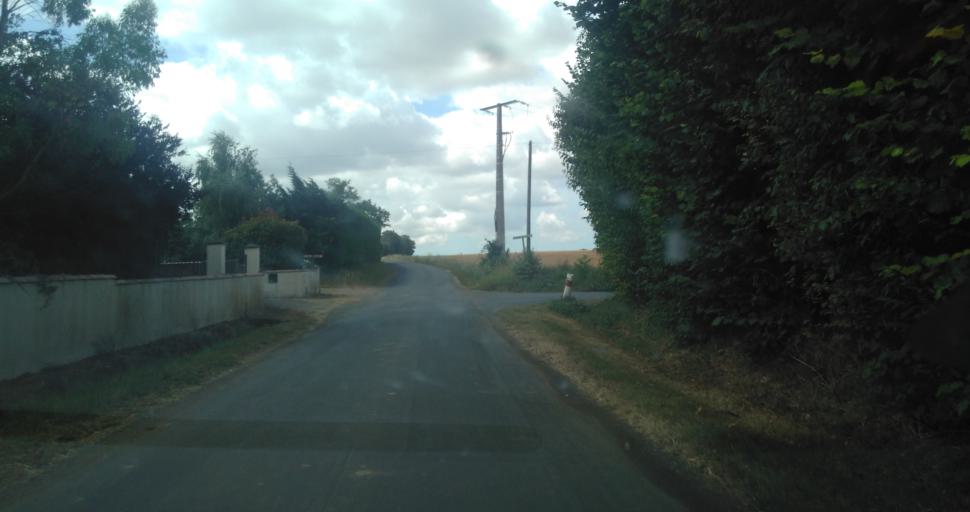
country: FR
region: Pays de la Loire
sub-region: Departement de la Vendee
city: Sainte-Hermine
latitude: 46.5332
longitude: -1.0854
